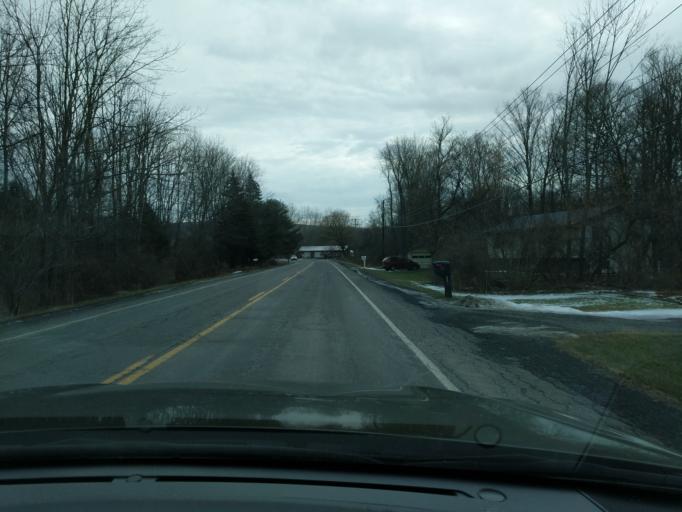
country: US
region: New York
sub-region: Tompkins County
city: East Ithaca
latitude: 42.3915
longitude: -76.4156
